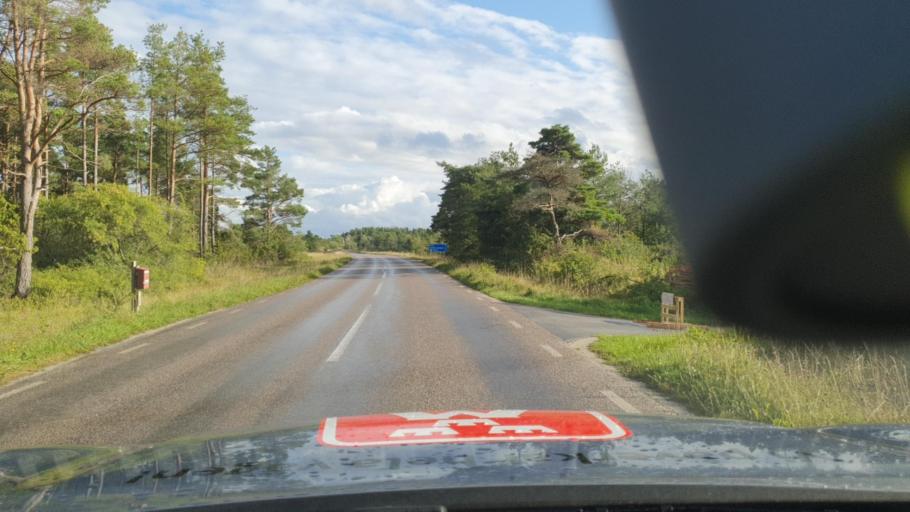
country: SE
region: Gotland
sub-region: Gotland
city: Slite
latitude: 57.6773
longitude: 18.7686
